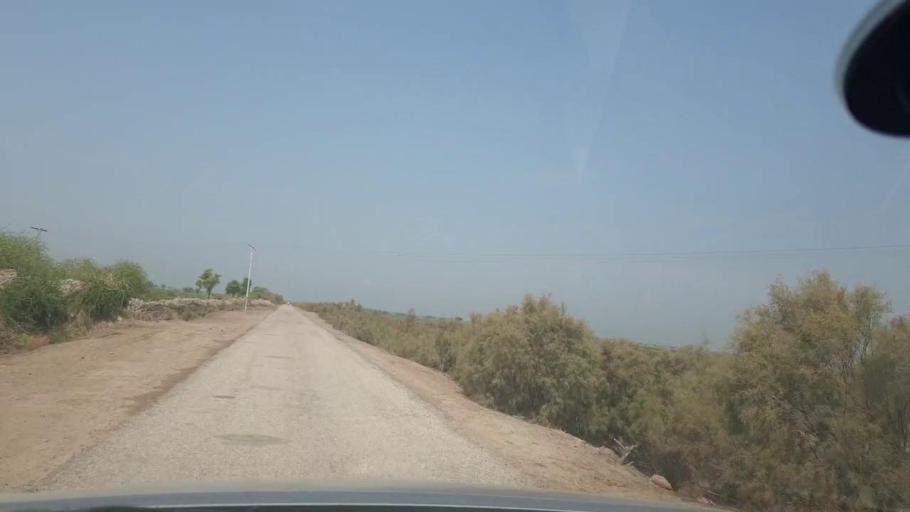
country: PK
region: Balochistan
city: Mehrabpur
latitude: 28.0581
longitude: 68.0741
